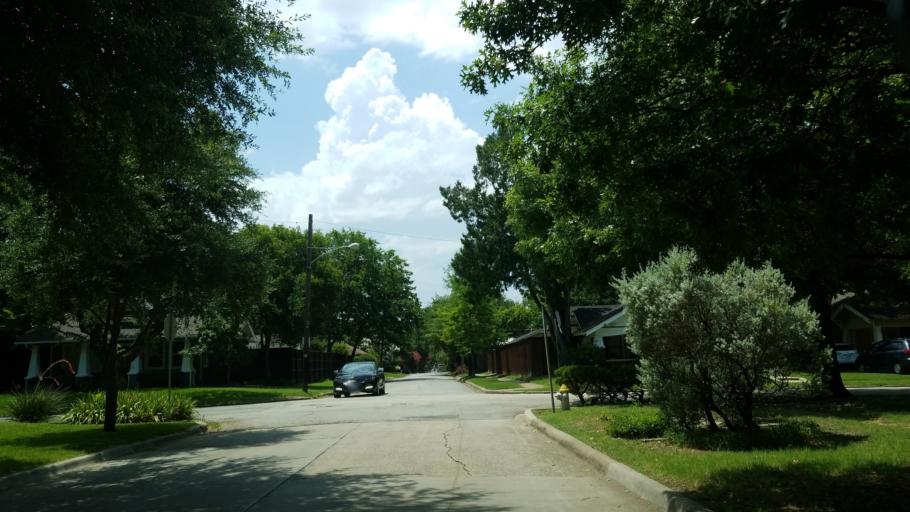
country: US
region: Texas
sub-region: Dallas County
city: Highland Park
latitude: 32.8237
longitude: -96.7775
